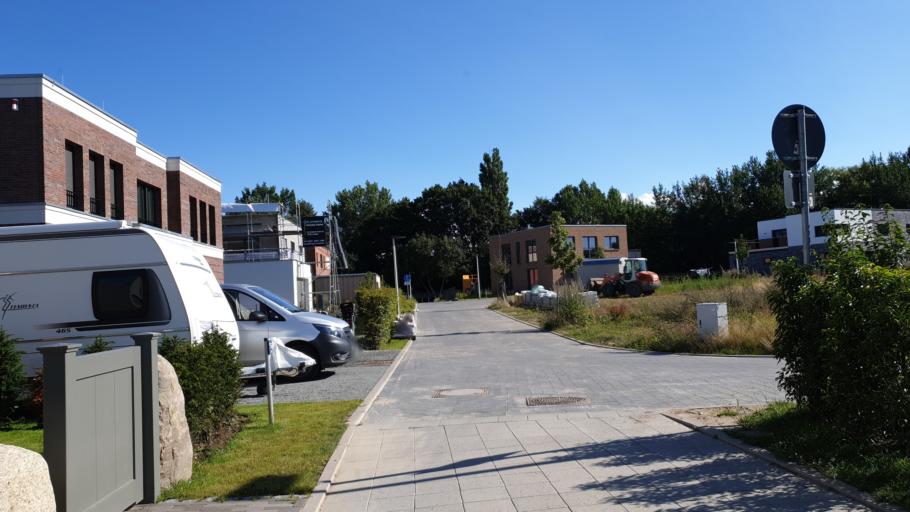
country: DE
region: Mecklenburg-Vorpommern
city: Kramerhof
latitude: 54.3420
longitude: 13.0738
